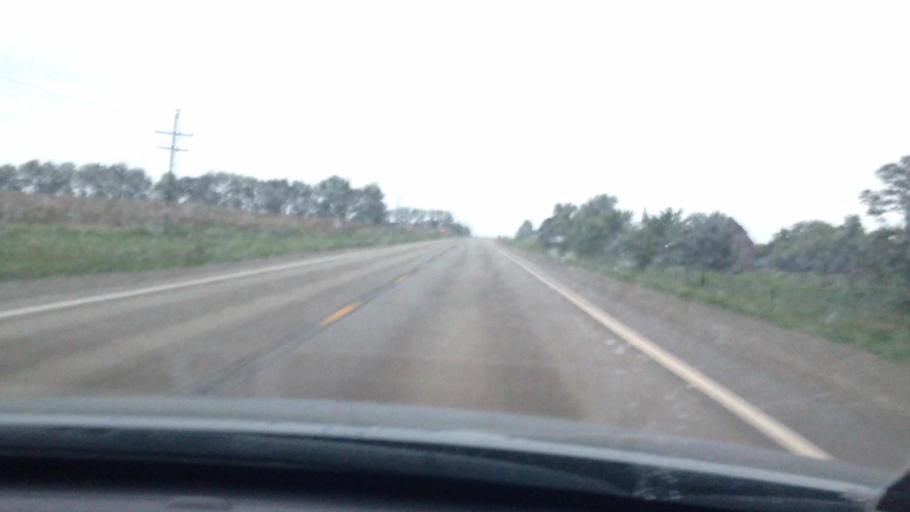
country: US
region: Kansas
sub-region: Brown County
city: Hiawatha
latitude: 39.8221
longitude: -95.5269
